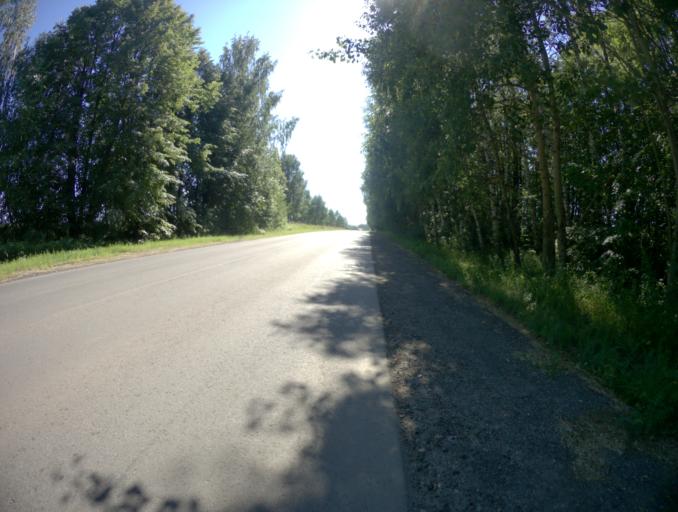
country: RU
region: Nizjnij Novgorod
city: Vorsma
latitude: 56.0378
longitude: 43.1916
